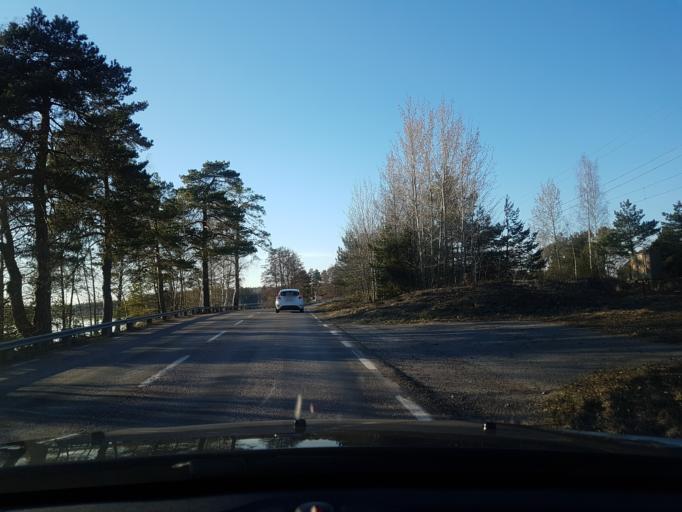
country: SE
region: Vaestmanland
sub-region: Sala Kommun
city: Sala
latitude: 59.9571
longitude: 16.5160
